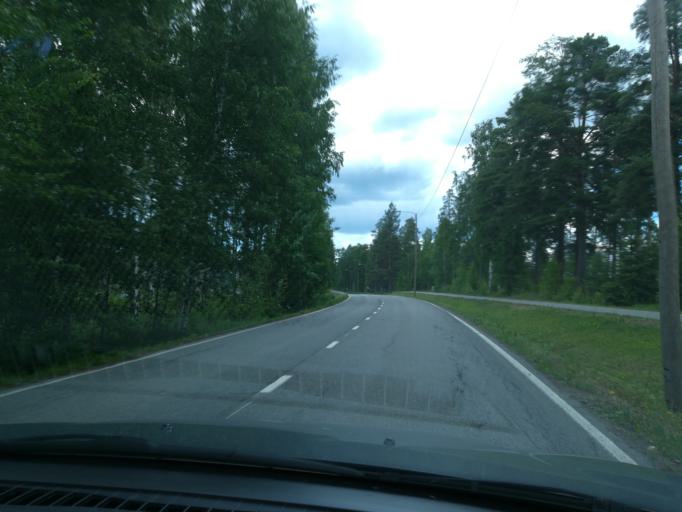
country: FI
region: Southern Savonia
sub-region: Mikkeli
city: Hirvensalmi
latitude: 61.6510
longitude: 26.7709
